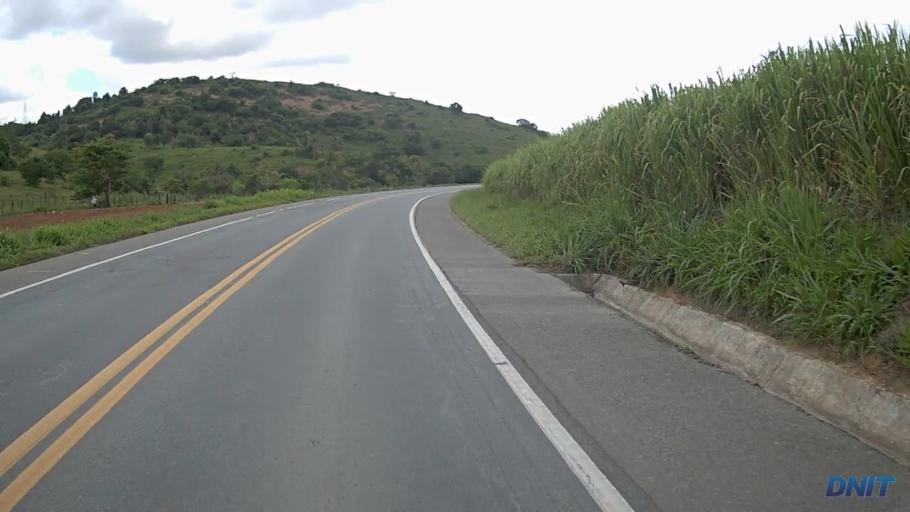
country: BR
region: Minas Gerais
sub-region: Governador Valadares
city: Governador Valadares
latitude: -18.9667
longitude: -42.0901
